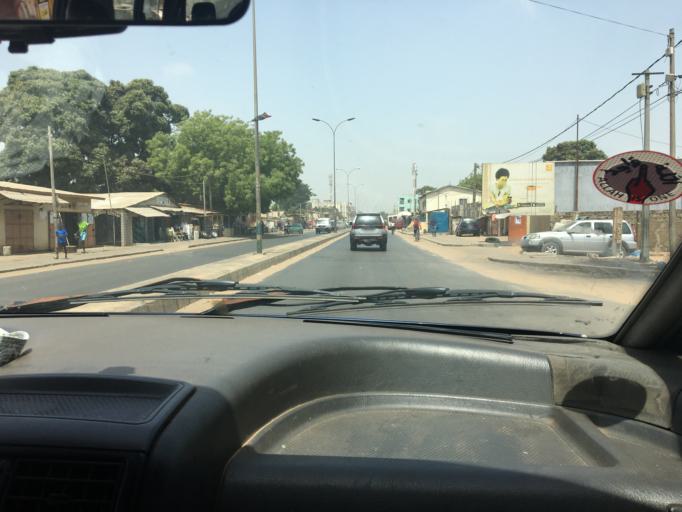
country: GM
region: Western
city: Abuko
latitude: 13.4086
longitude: -16.6677
